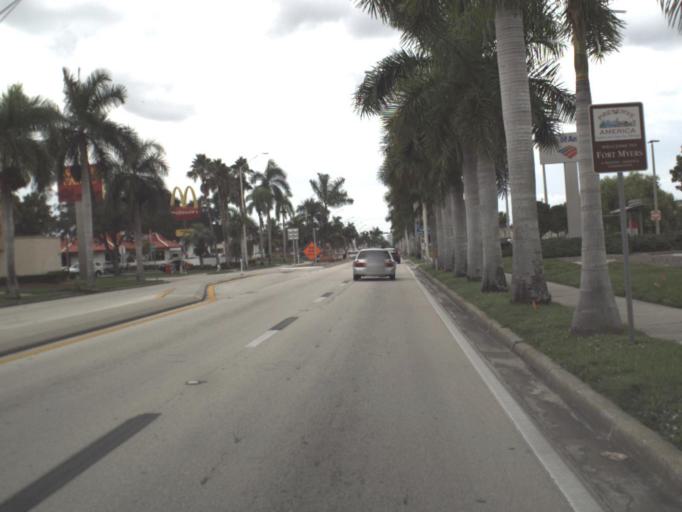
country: US
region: Florida
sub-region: Lee County
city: Tice
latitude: 26.6689
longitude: -81.8260
